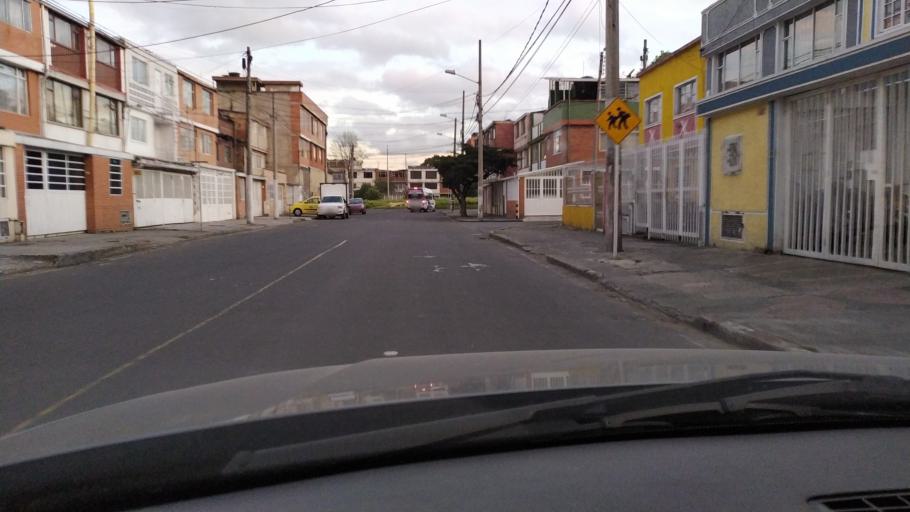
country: CO
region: Bogota D.C.
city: Bogota
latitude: 4.6149
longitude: -74.1121
